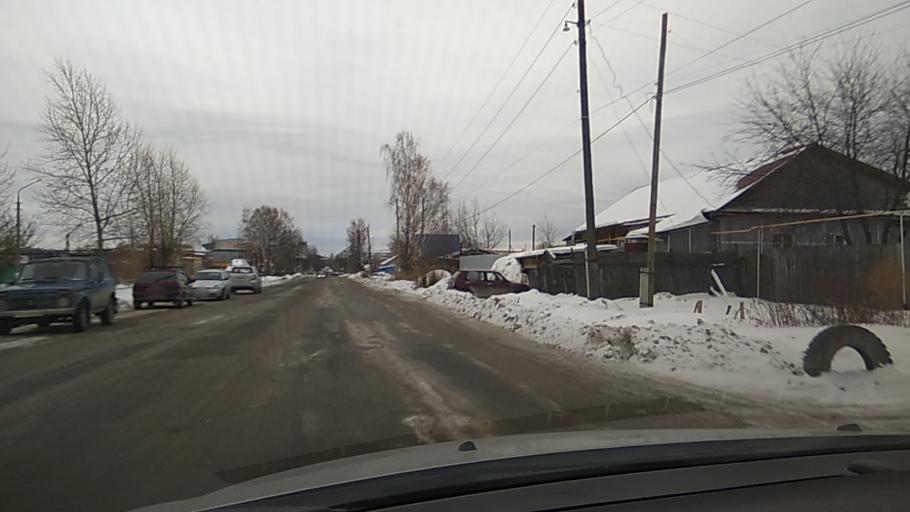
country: RU
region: Sverdlovsk
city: Revda
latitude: 56.8089
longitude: 59.9358
